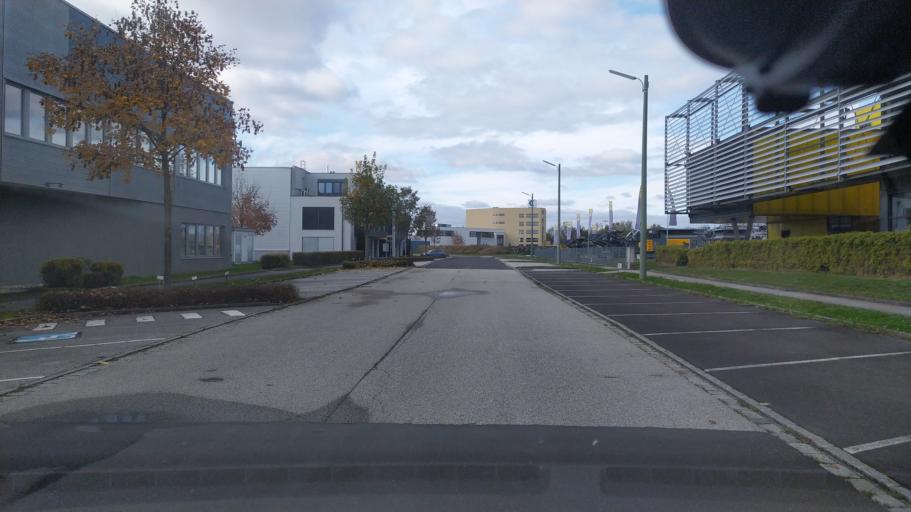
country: AT
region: Upper Austria
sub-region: Politischer Bezirk Urfahr-Umgebung
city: Steyregg
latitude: 48.2538
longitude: 14.3789
